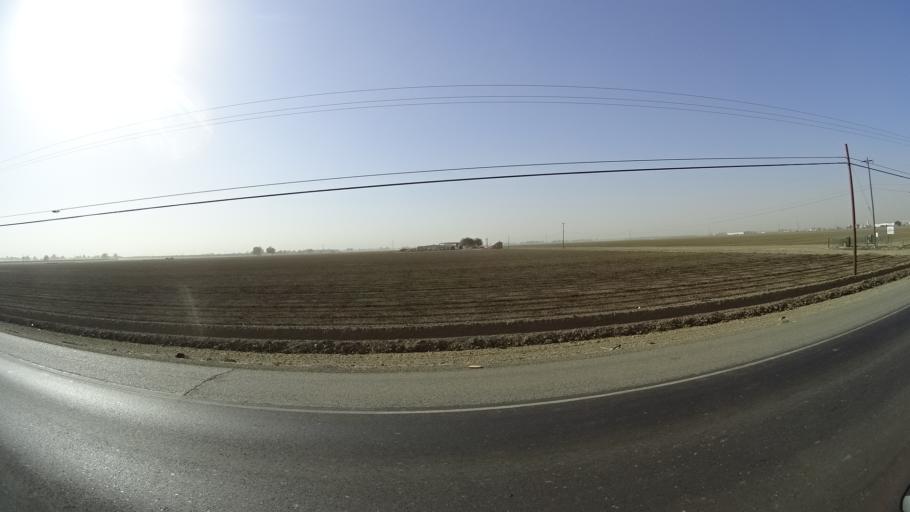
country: US
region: California
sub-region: Yolo County
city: Woodland
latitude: 38.7413
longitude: -121.7295
